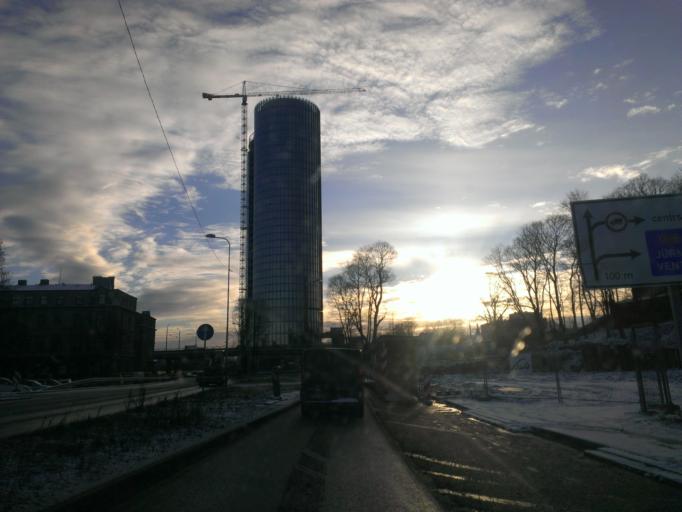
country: LV
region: Riga
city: Riga
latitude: 56.9491
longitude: 24.0770
